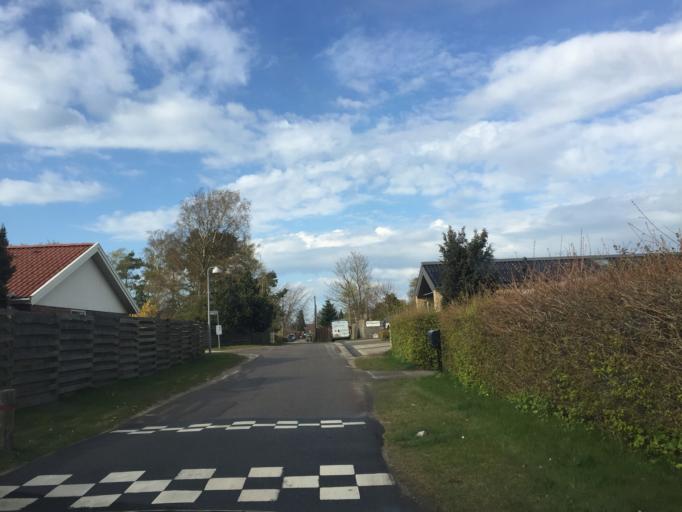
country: DK
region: Capital Region
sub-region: Halsnaes Kommune
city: Liseleje
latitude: 56.0067
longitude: 11.9936
